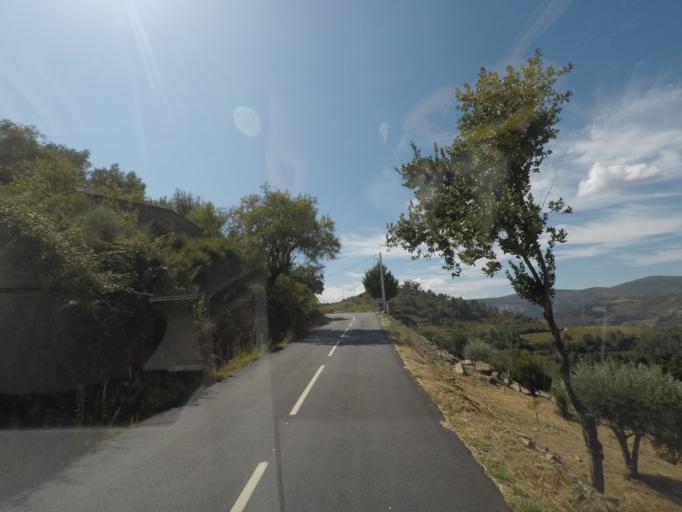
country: PT
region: Vila Real
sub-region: Sabrosa
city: Sabrosa
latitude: 41.2173
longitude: -7.5265
